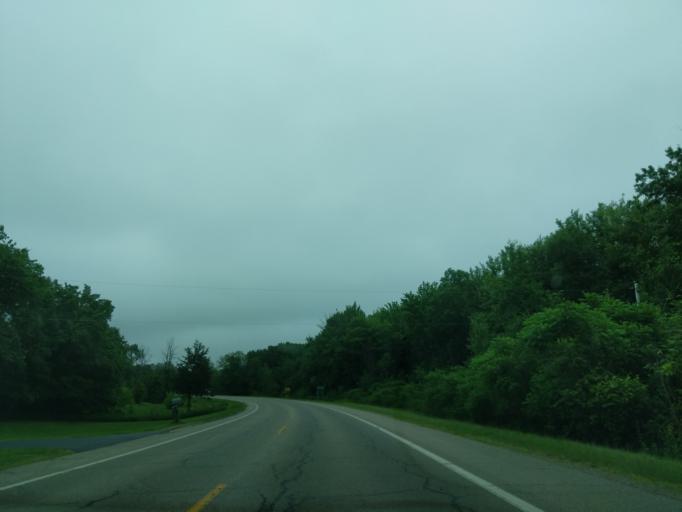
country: US
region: Michigan
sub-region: Hillsdale County
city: Litchfield
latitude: 42.0312
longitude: -84.7323
